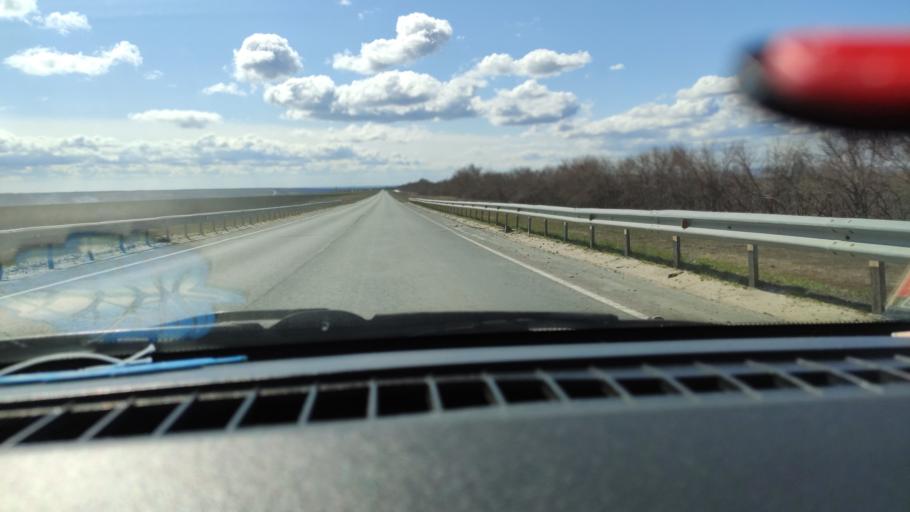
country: RU
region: Saratov
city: Dukhovnitskoye
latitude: 52.7752
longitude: 48.2348
